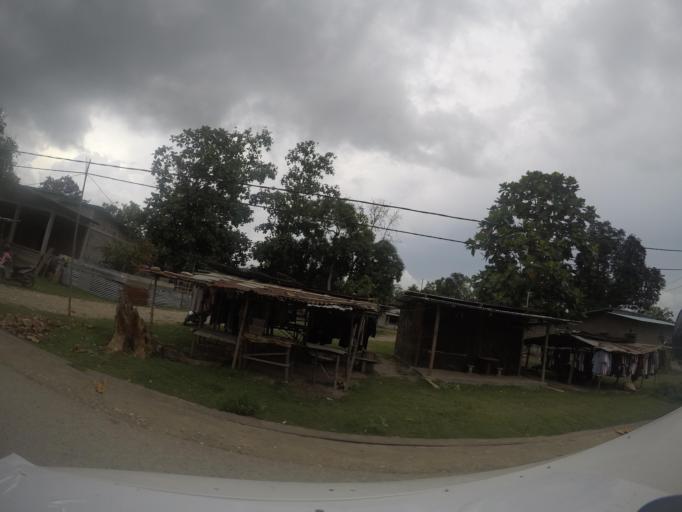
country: TL
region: Viqueque
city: Viqueque
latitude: -8.8574
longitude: 126.3633
